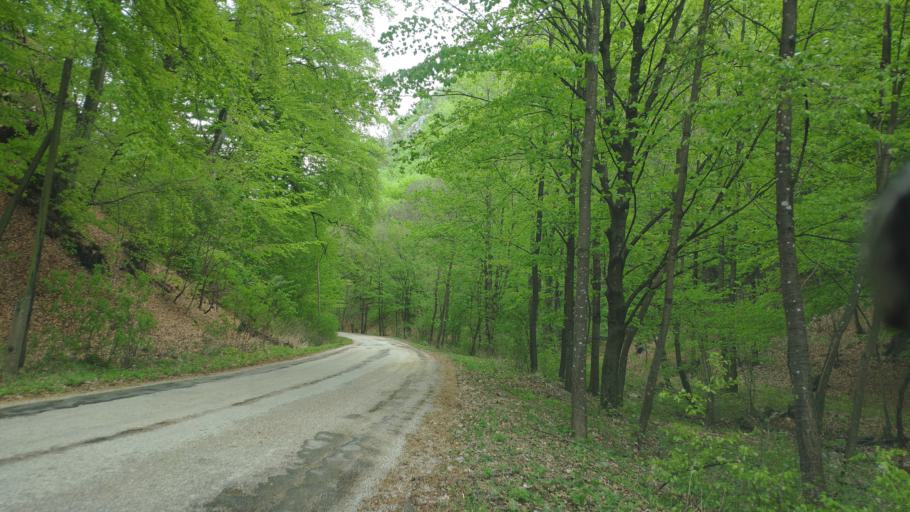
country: SK
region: Kosicky
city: Medzev
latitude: 48.6494
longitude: 20.8464
